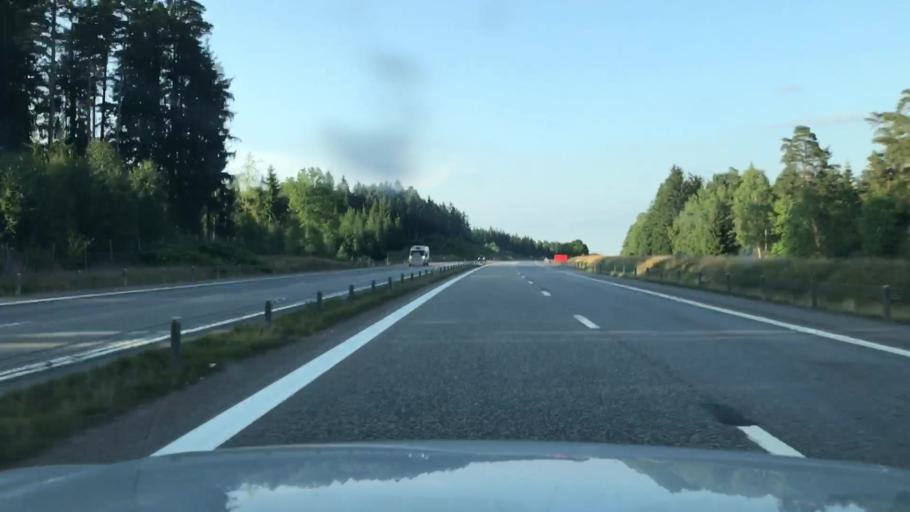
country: SE
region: Kronoberg
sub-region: Markaryds Kommun
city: Stromsnasbruk
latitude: 56.5290
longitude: 13.6866
